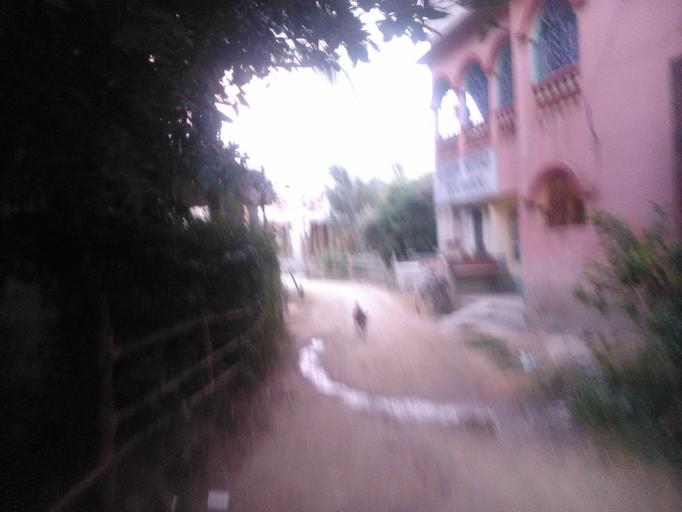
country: IN
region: West Bengal
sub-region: Nadia
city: Navadwip
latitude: 23.4323
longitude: 88.3890
